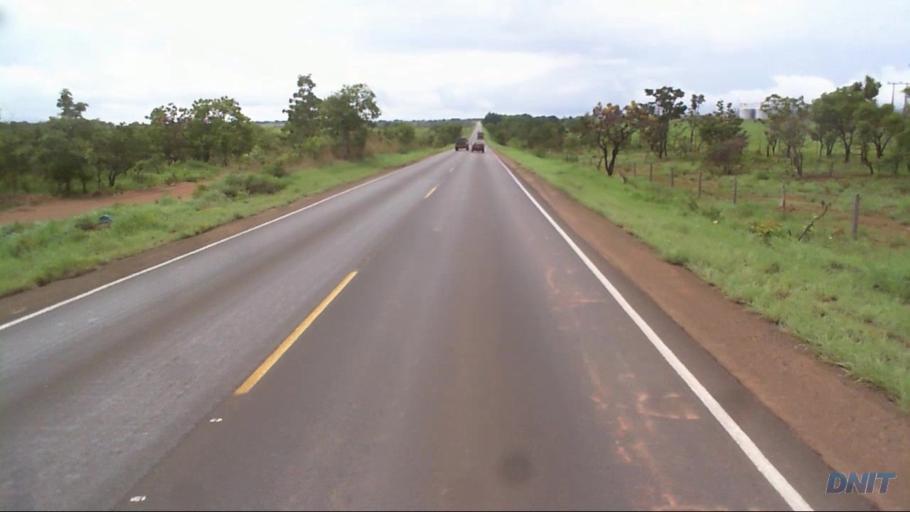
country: BR
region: Goias
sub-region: Padre Bernardo
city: Padre Bernardo
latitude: -15.2315
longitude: -48.2759
